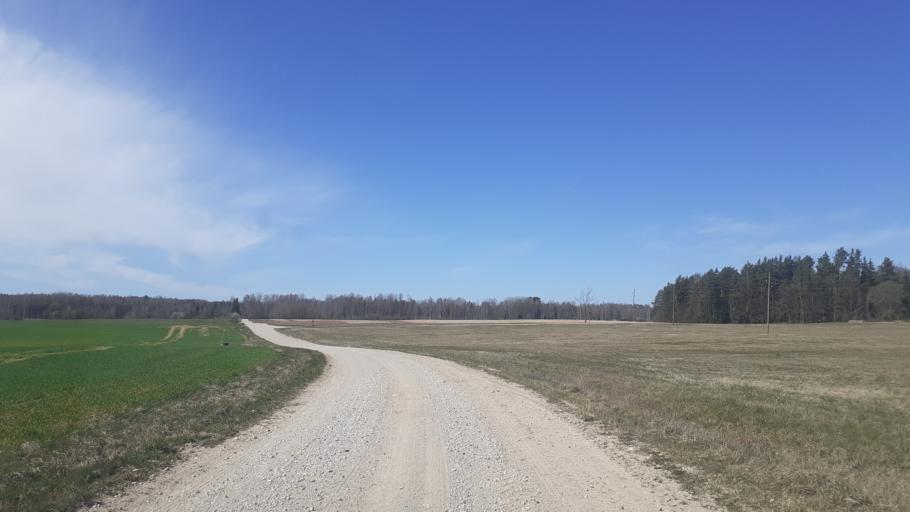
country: LV
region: Kuldigas Rajons
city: Kuldiga
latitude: 56.8405
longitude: 21.9890
